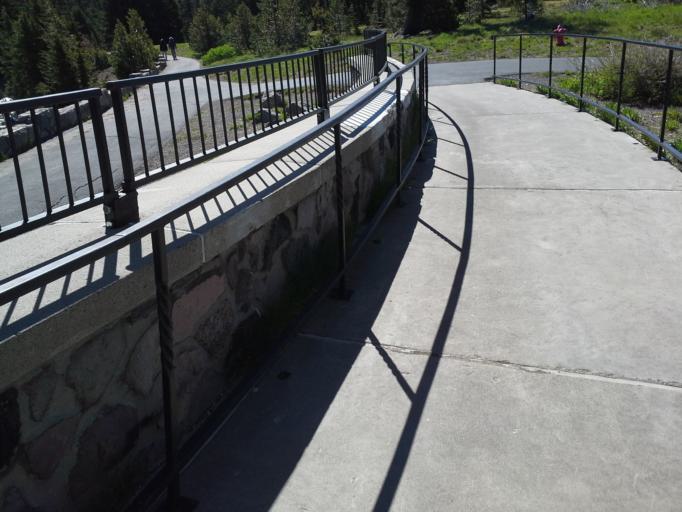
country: US
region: Oregon
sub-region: Jackson County
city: Shady Cove
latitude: 42.9097
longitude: -122.1405
